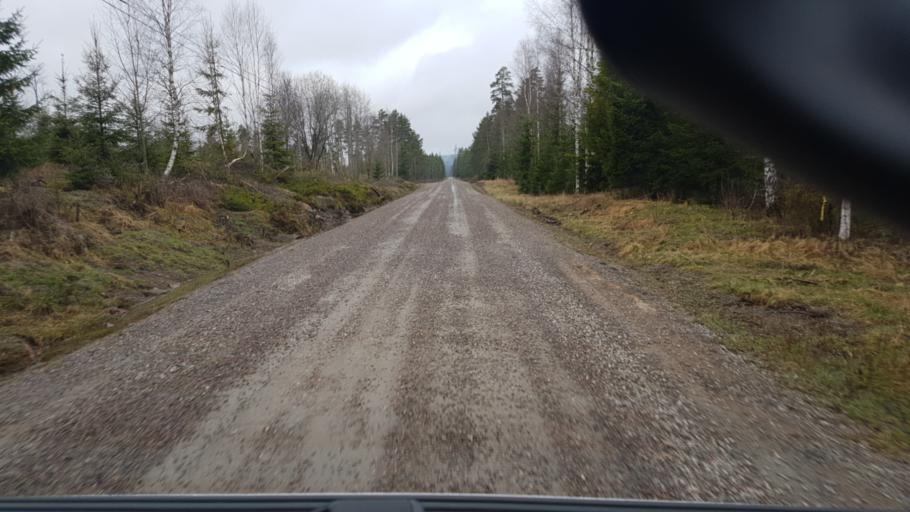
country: SE
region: Vaermland
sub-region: Eda Kommun
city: Charlottenberg
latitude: 59.9524
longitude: 12.5153
